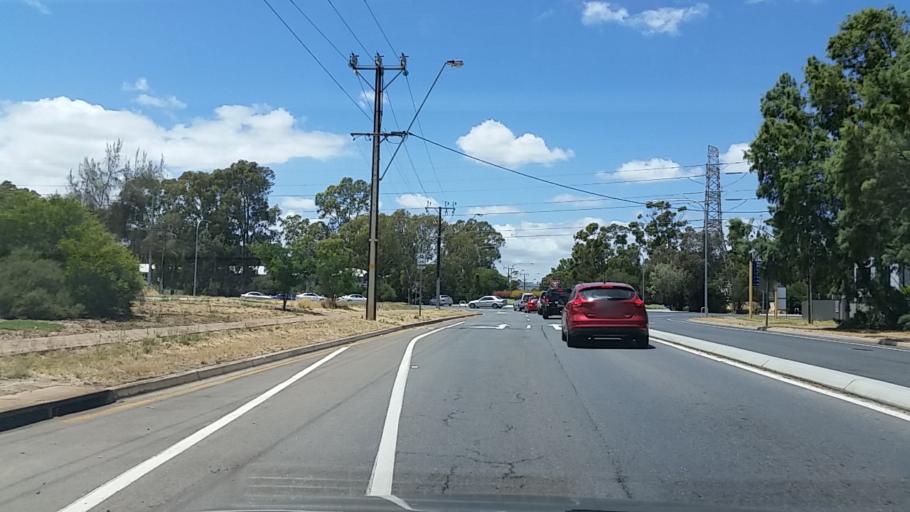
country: AU
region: South Australia
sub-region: Salisbury
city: Salisbury
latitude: -34.7724
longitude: 138.6152
